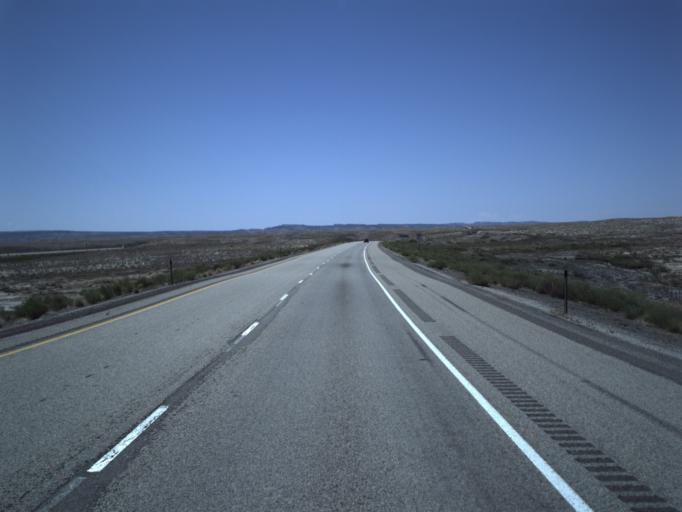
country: US
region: Utah
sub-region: Grand County
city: Moab
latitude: 38.9857
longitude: -109.3404
